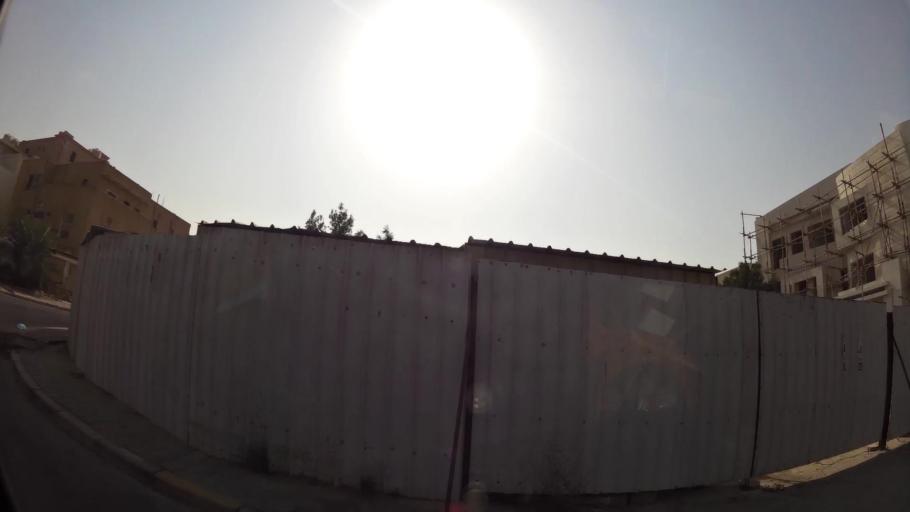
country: KW
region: Muhafazat al Jahra'
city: Al Jahra'
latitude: 29.3579
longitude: 47.6742
